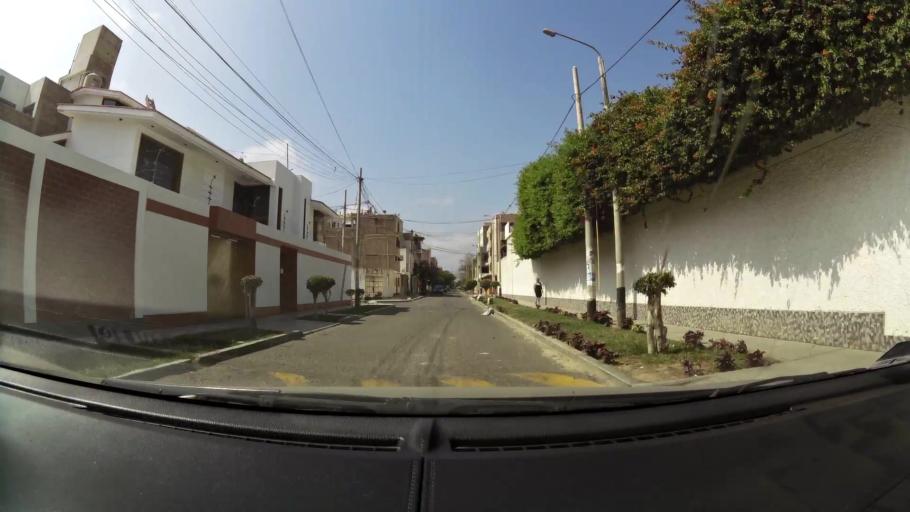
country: PE
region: La Libertad
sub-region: Provincia de Trujillo
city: Buenos Aires
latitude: -8.1287
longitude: -79.0463
